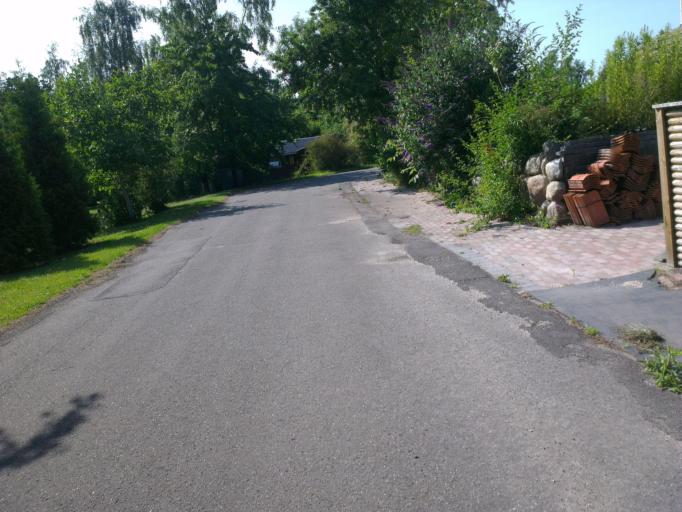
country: DK
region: Capital Region
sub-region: Halsnaes Kommune
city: Hundested
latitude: 55.9252
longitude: 11.9249
